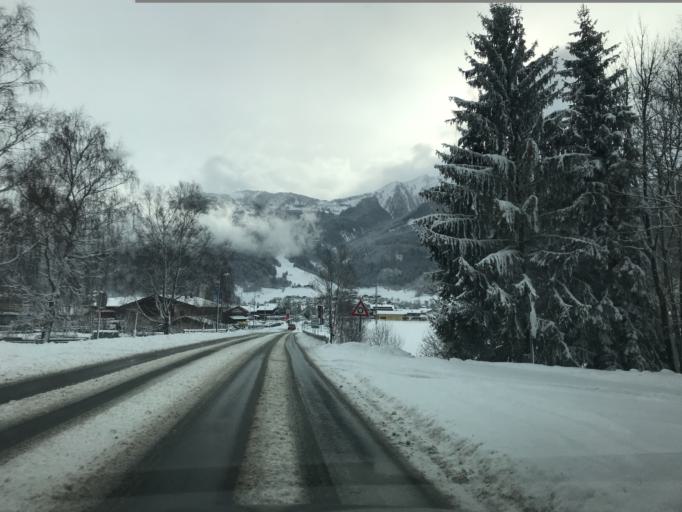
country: AT
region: Salzburg
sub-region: Politischer Bezirk Zell am See
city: Kaprun
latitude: 47.2840
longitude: 12.7522
